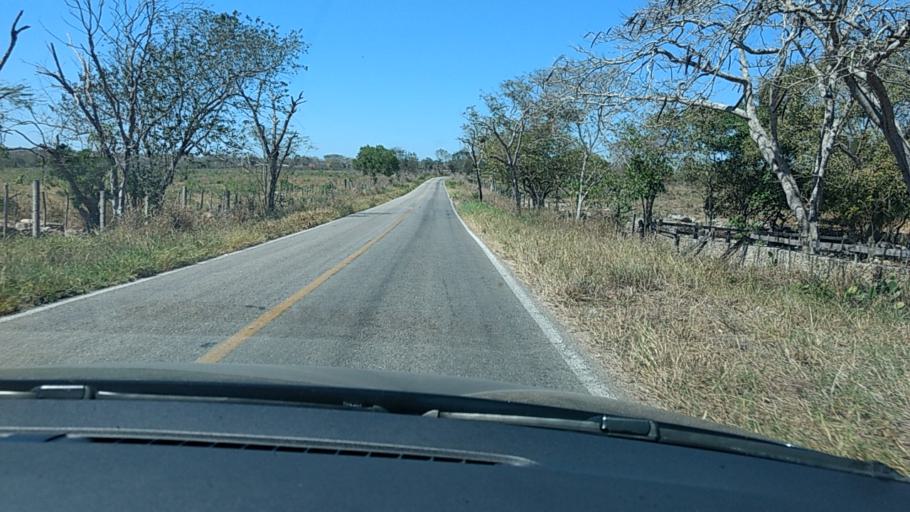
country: MX
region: Yucatan
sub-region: Tizimin
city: Tizimin
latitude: 21.1965
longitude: -88.1779
